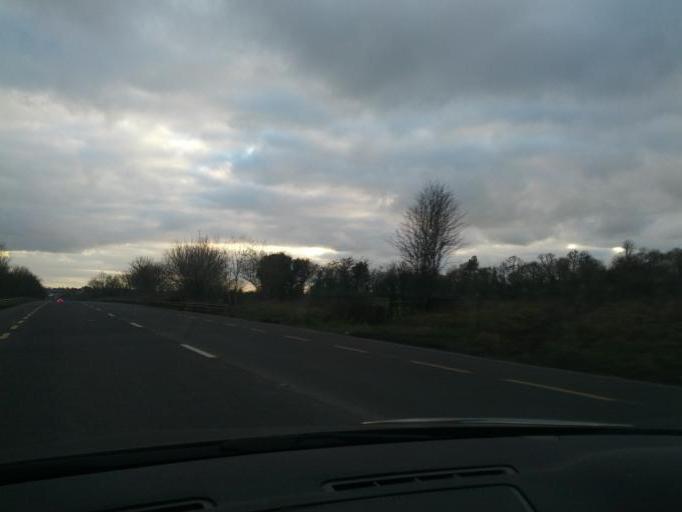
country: IE
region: Leinster
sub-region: Uibh Fhaili
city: Birr
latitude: 53.1133
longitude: -7.8948
